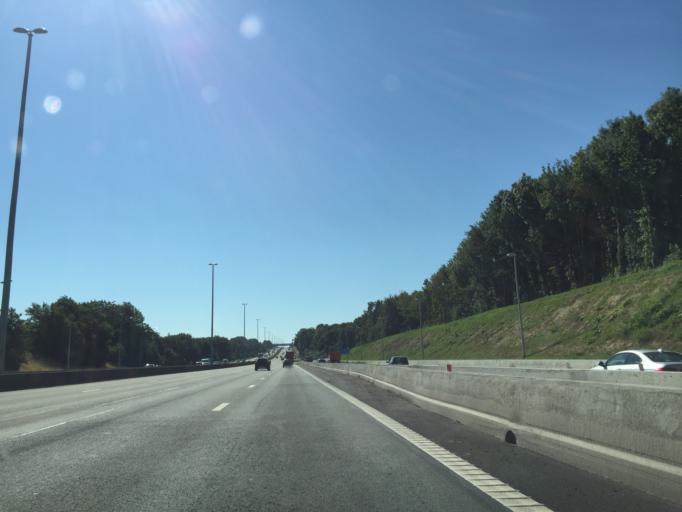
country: BE
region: Wallonia
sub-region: Province de Liege
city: Blegny
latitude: 50.6662
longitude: 5.6921
